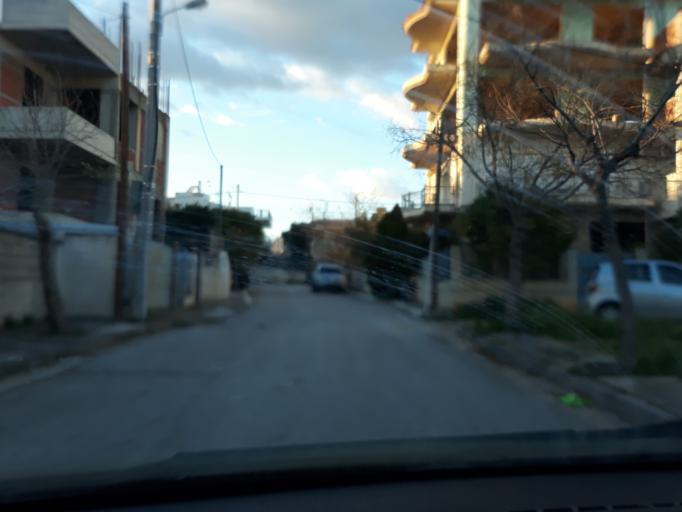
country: GR
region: Attica
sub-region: Nomarchia Dytikis Attikis
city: Ano Liosia
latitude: 38.0835
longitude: 23.7028
